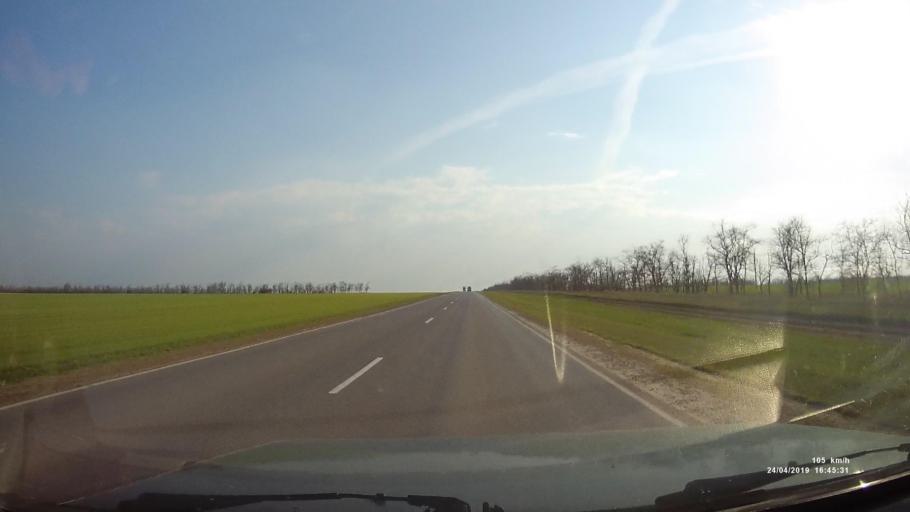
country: RU
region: Rostov
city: Gundorovskiy
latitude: 46.7686
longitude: 41.8134
